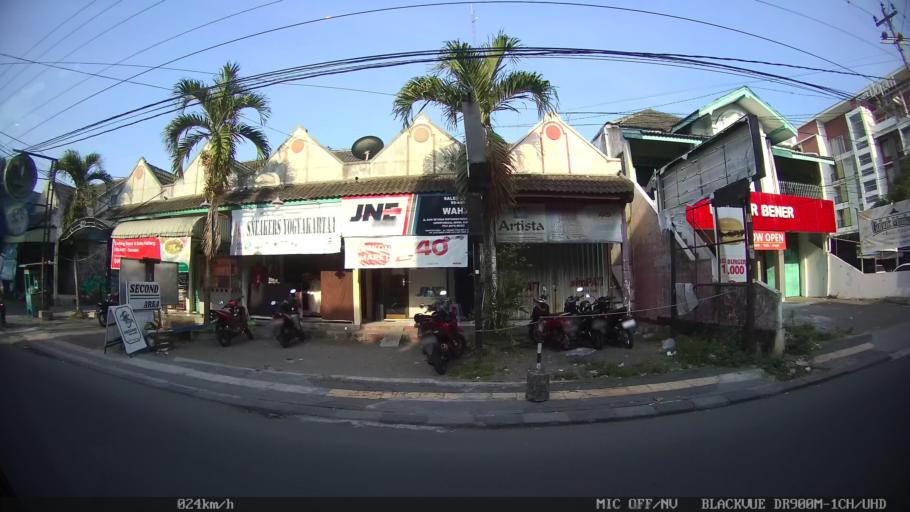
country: ID
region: Daerah Istimewa Yogyakarta
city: Depok
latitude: -7.7652
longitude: 110.4111
